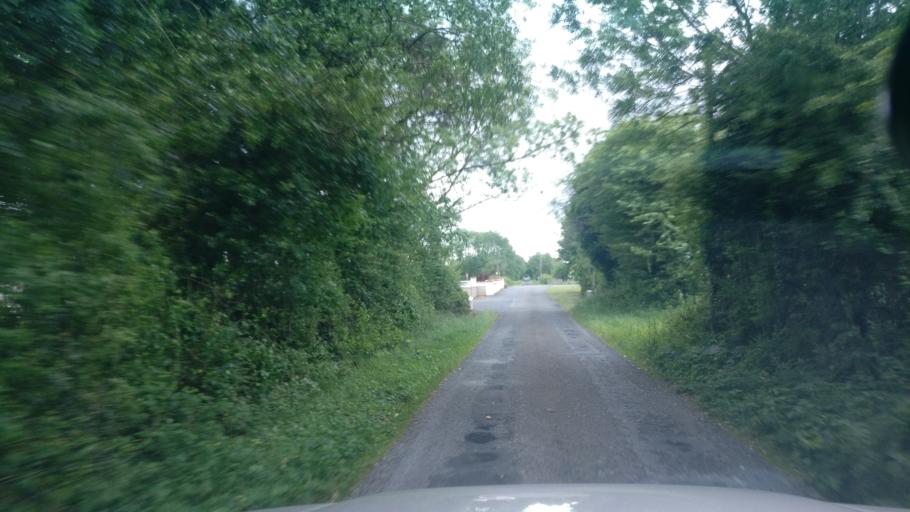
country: IE
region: Connaught
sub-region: County Galway
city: Portumna
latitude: 53.1877
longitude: -8.3260
